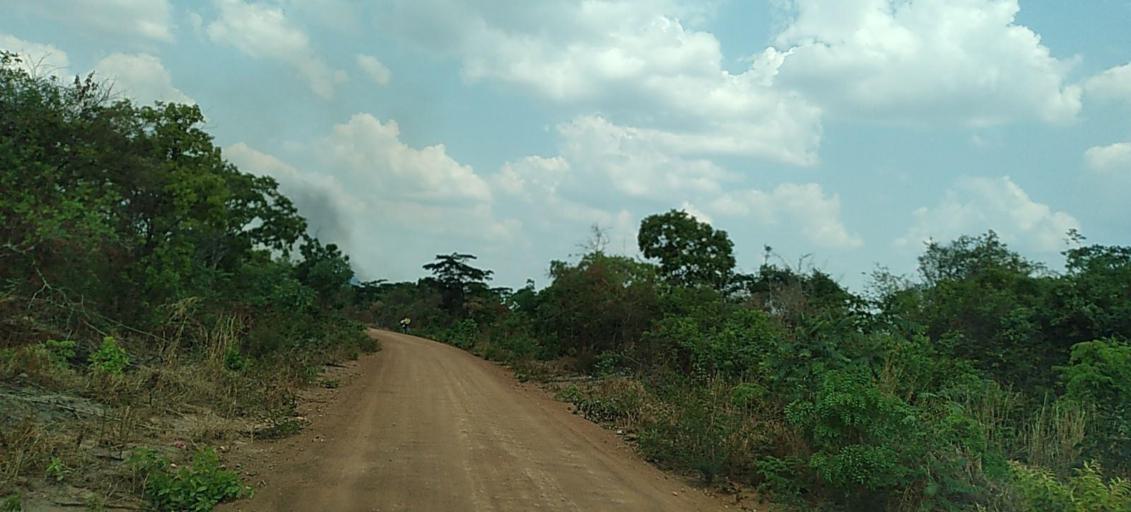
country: ZM
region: Copperbelt
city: Luanshya
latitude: -13.1404
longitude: 28.3328
